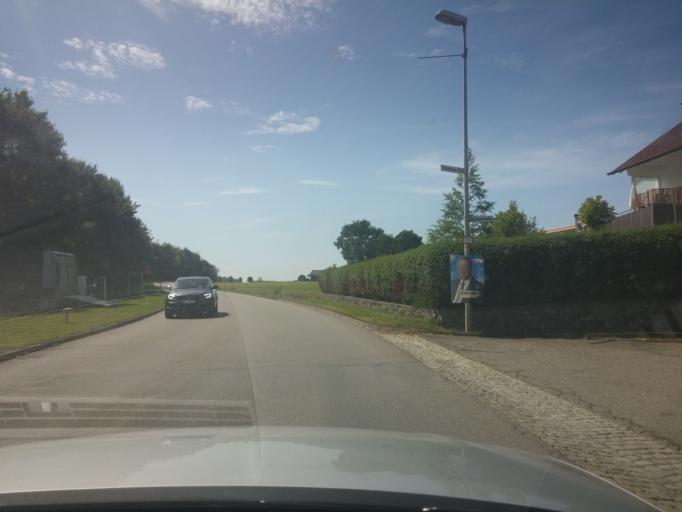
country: DE
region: Baden-Wuerttemberg
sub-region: Tuebingen Region
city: Ingoldingen
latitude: 48.0255
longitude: 9.7358
